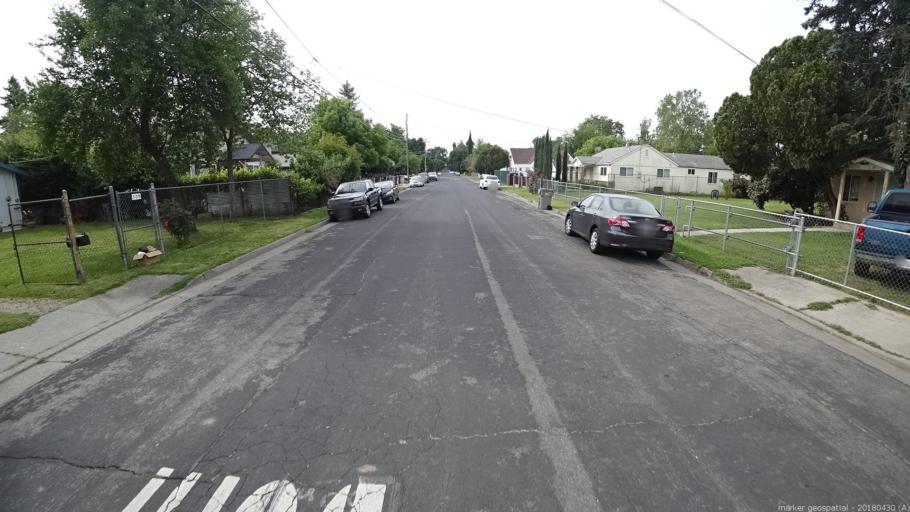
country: US
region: California
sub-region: Yolo County
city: West Sacramento
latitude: 38.5986
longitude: -121.5376
